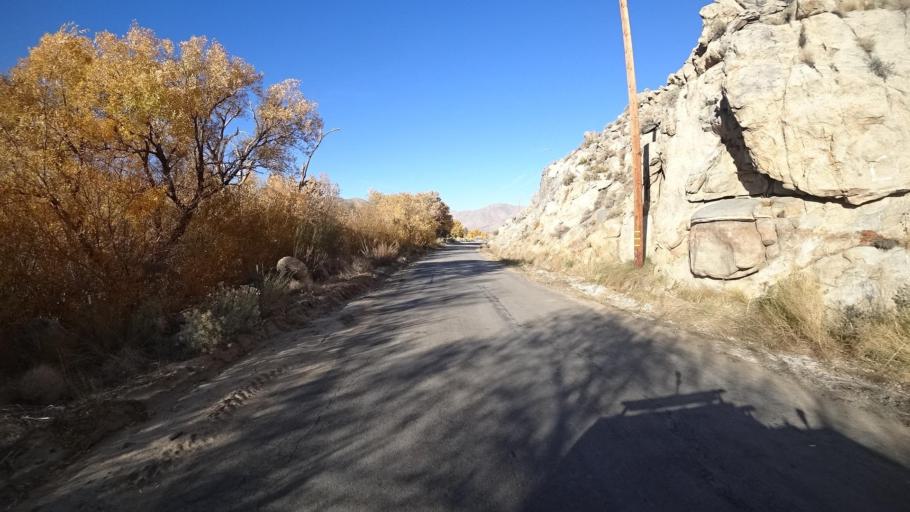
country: US
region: California
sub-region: Kern County
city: Weldon
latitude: 35.5771
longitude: -118.2506
